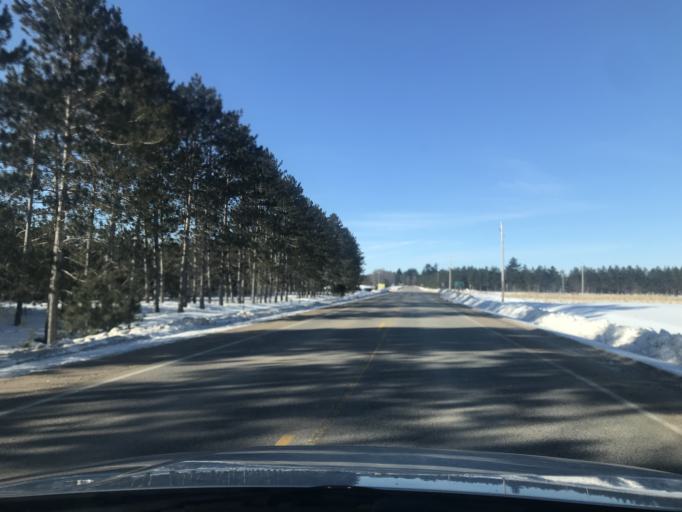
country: US
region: Wisconsin
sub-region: Marinette County
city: Niagara
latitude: 45.4292
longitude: -88.0347
